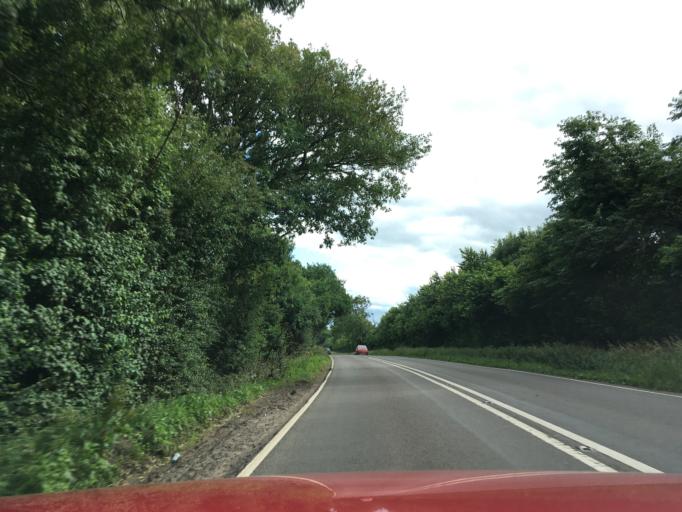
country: GB
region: England
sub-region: Leicestershire
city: Measham
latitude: 52.6653
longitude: -1.5390
